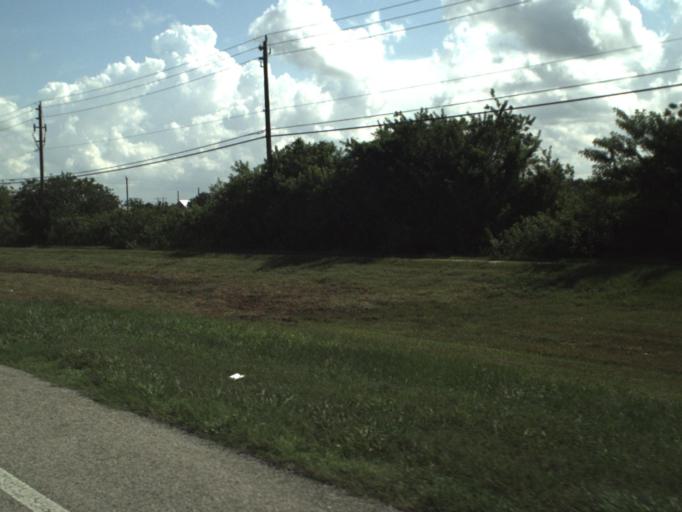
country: US
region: Florida
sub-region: Palm Beach County
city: Villages of Oriole
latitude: 26.5172
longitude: -80.2054
